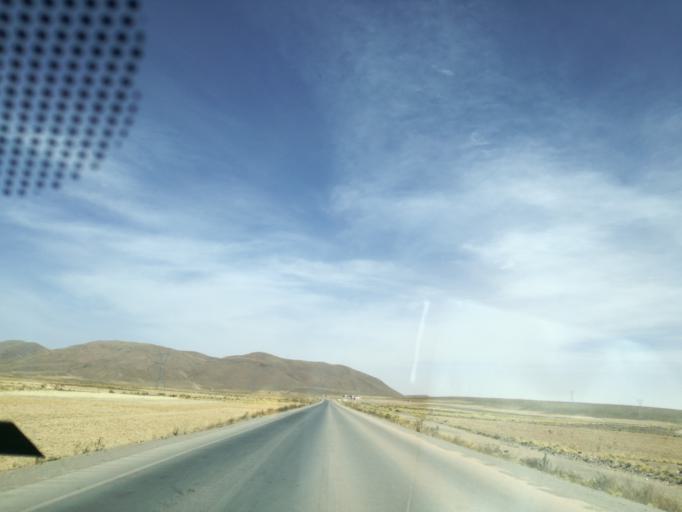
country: BO
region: Oruro
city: Oruro
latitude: -17.8542
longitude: -67.0248
